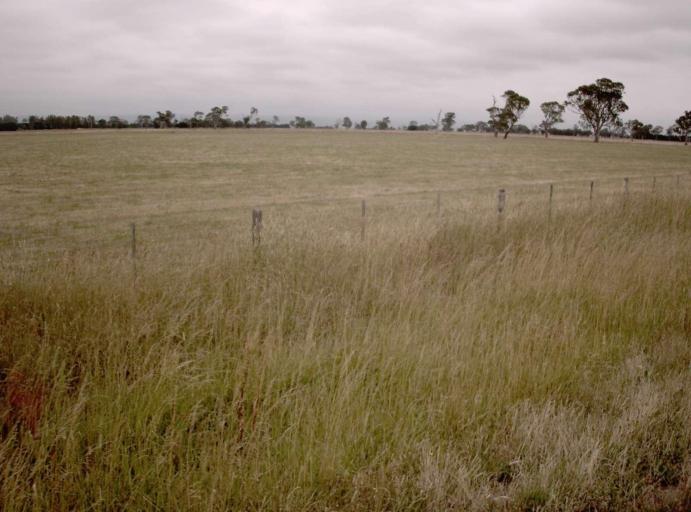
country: AU
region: Victoria
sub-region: Wellington
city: Heyfield
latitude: -38.0608
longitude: 146.7692
